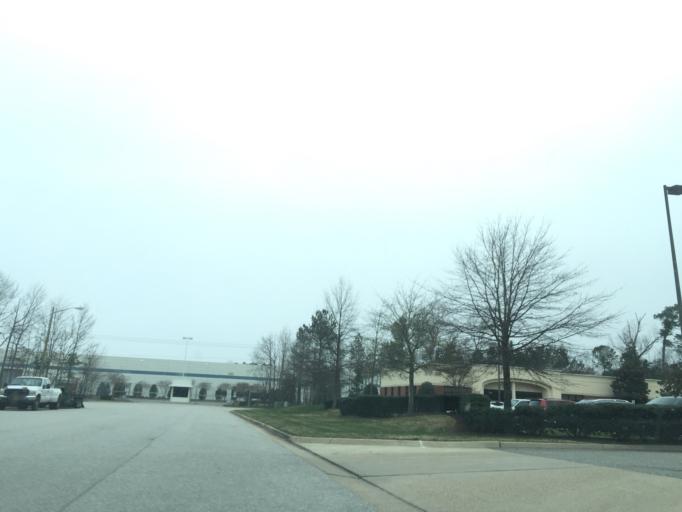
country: US
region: Virginia
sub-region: City of Newport News
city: Newport News
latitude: 37.0963
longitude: -76.4681
